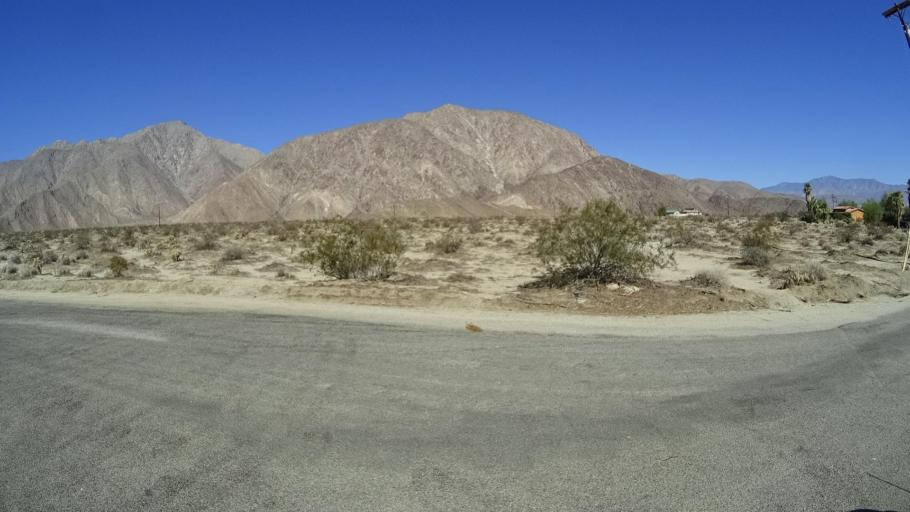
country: US
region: California
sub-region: San Diego County
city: Borrego Springs
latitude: 33.2757
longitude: -116.3944
